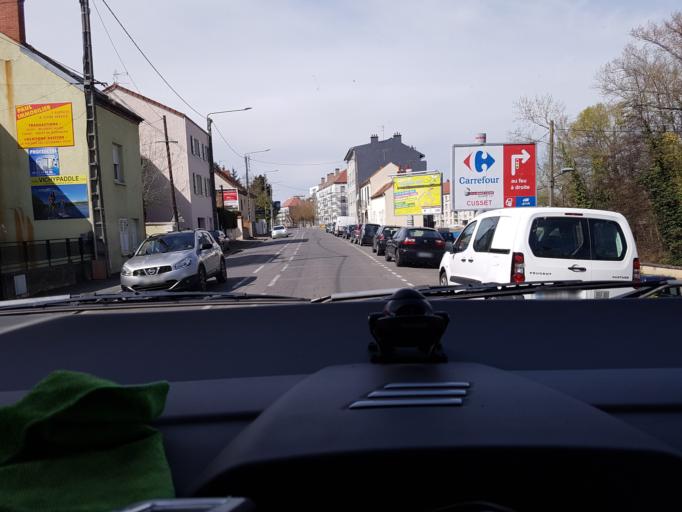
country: FR
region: Auvergne
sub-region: Departement de l'Allier
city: Cusset
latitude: 46.1345
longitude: 3.4439
